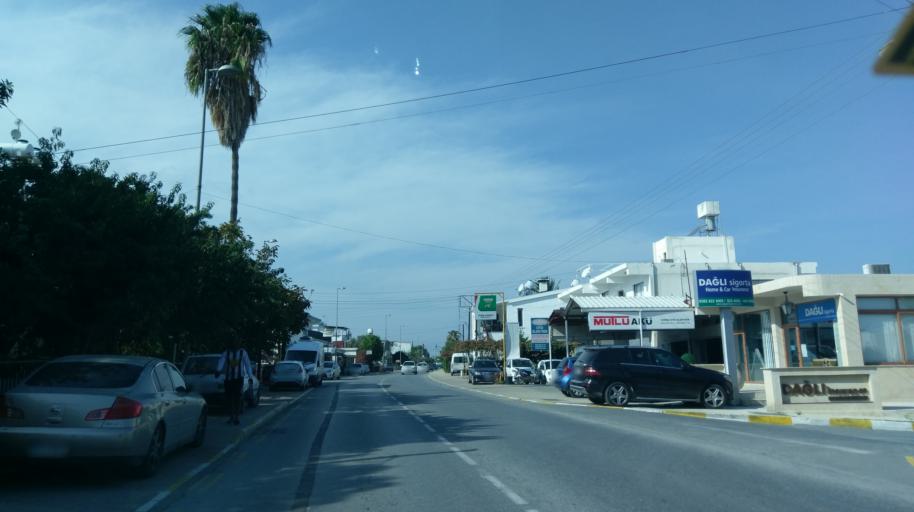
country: CY
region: Keryneia
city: Kyrenia
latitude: 35.3426
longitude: 33.2707
